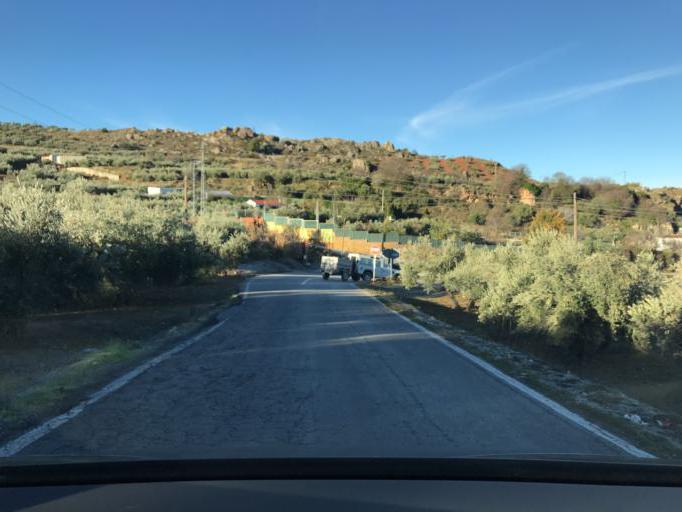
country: ES
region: Andalusia
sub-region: Provincia de Granada
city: Nivar
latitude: 37.2636
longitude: -3.5779
